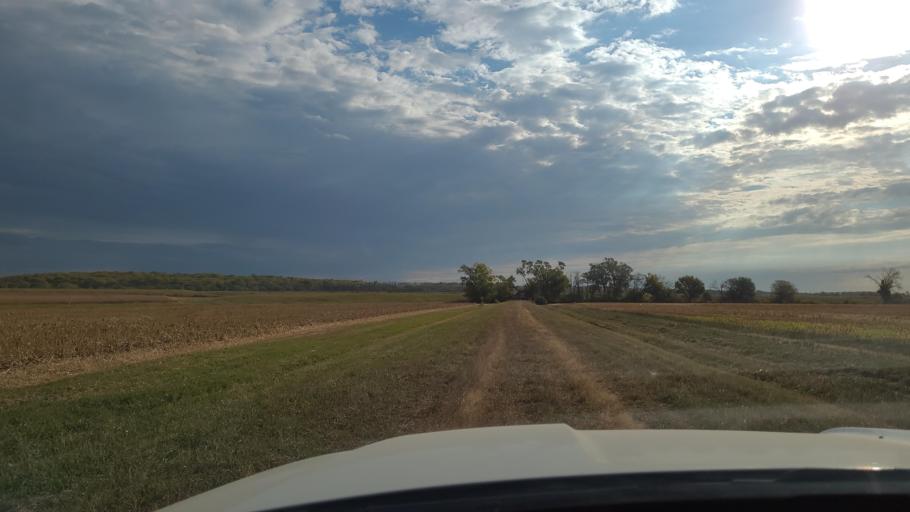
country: US
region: Kansas
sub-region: Douglas County
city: Lawrence
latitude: 39.0151
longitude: -95.2232
